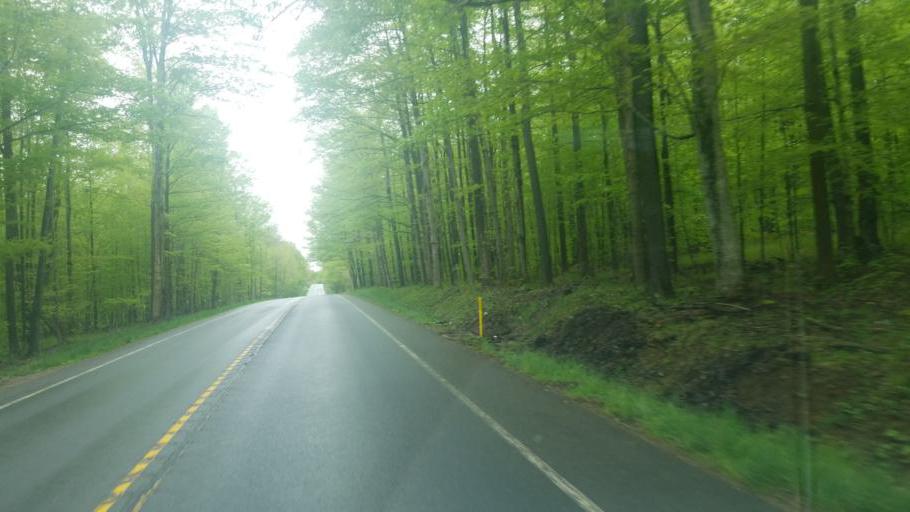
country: US
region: Pennsylvania
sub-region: McKean County
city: Kane
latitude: 41.5889
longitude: -78.8443
